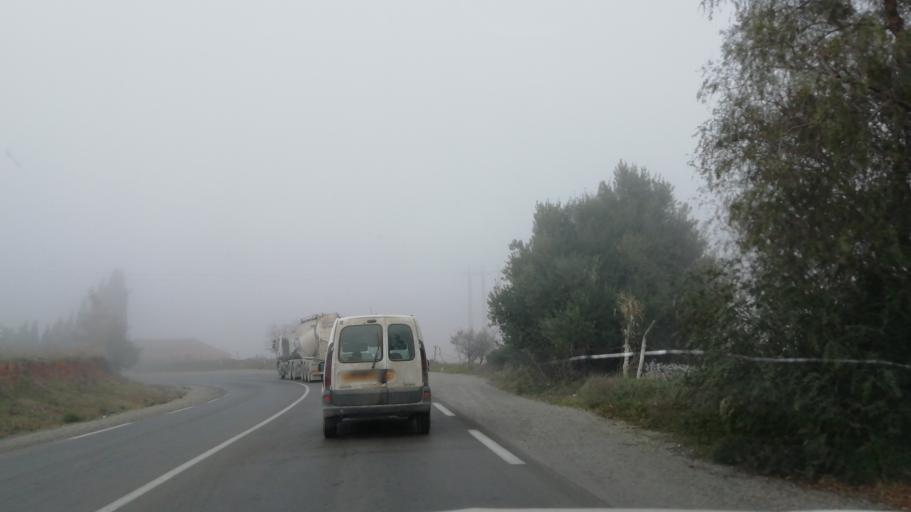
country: DZ
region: Mascara
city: Mascara
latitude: 35.5211
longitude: 0.3179
